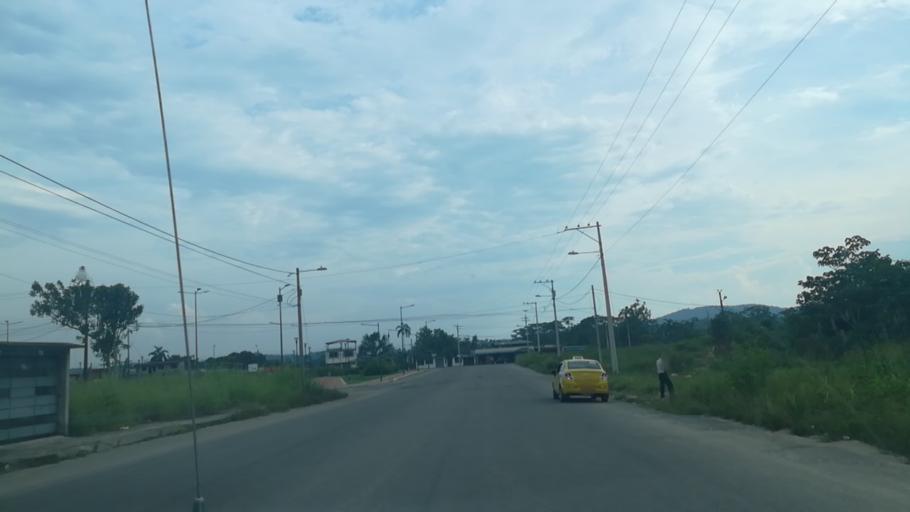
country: EC
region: Napo
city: Tena
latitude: -0.9845
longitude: -77.8241
